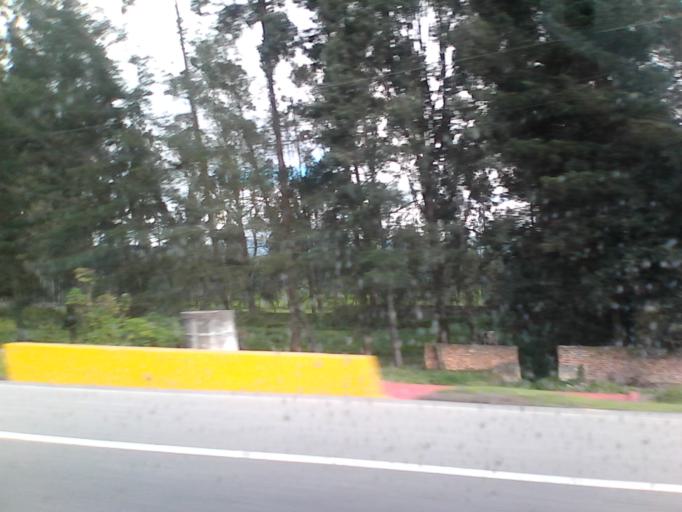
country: CO
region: Cundinamarca
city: Cajica
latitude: 4.8799
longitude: -74.0177
